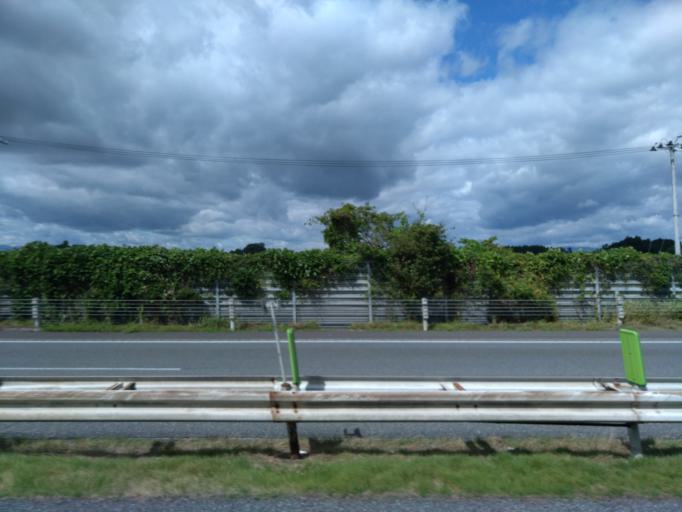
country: JP
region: Miyagi
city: Furukawa
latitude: 38.6182
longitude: 140.9456
